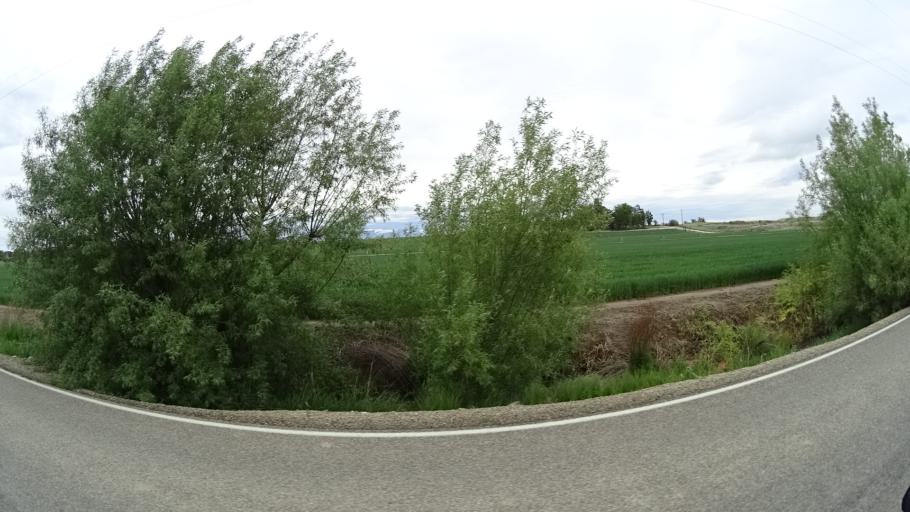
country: US
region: Idaho
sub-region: Ada County
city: Star
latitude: 43.7153
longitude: -116.4685
